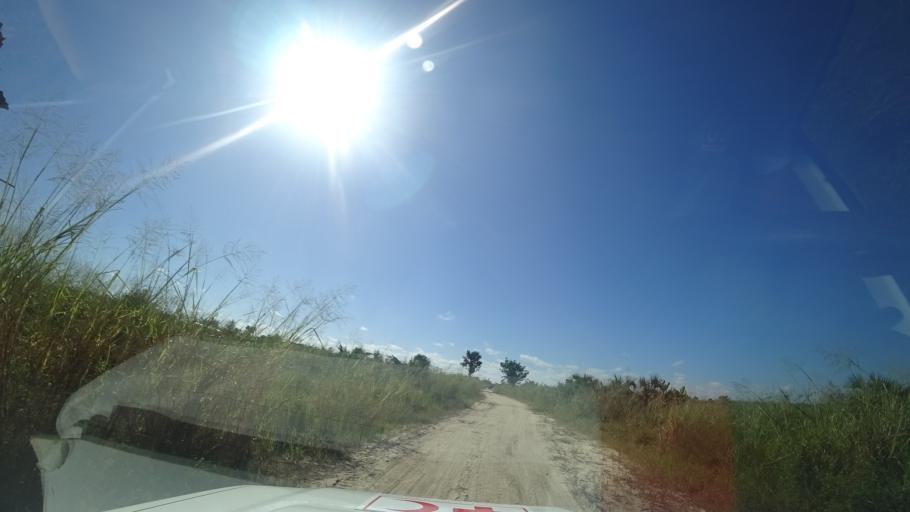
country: MZ
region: Sofala
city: Dondo
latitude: -19.3871
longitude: 34.5880
